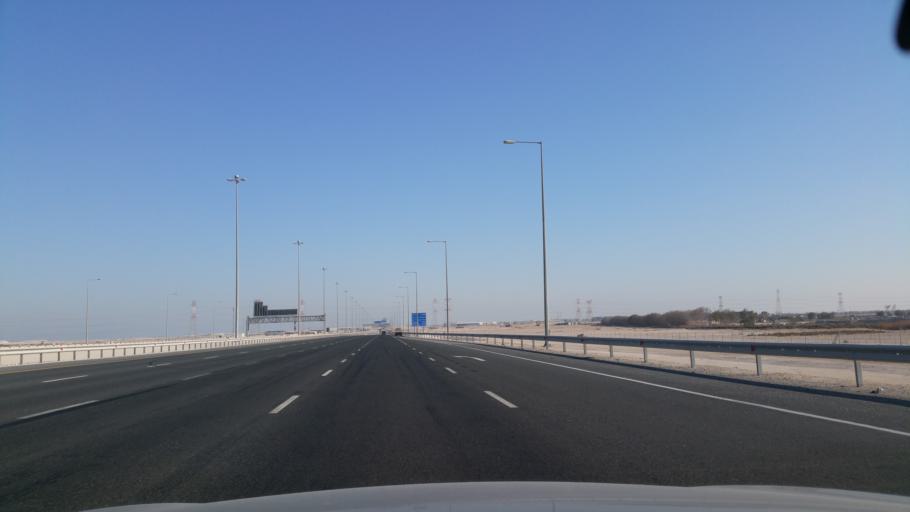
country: QA
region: Al Wakrah
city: Al Wukayr
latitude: 25.1117
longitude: 51.4979
